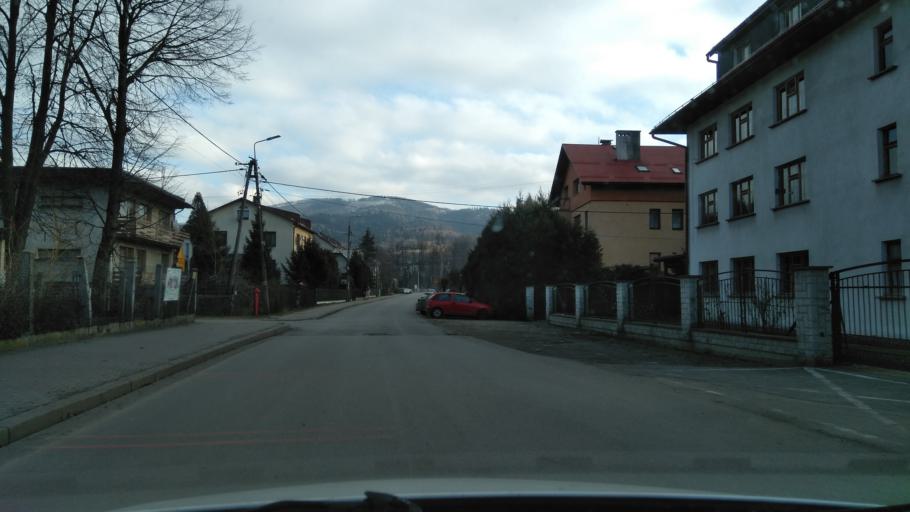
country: PL
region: Silesian Voivodeship
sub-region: Powiat zywiecki
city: Milowka
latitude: 49.5579
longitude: 19.0888
